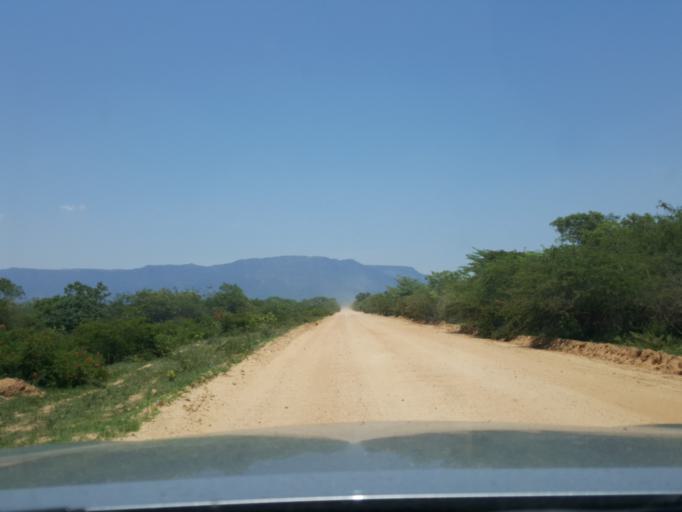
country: ZA
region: Limpopo
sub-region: Mopani District Municipality
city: Hoedspruit
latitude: -24.5668
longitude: 31.0082
